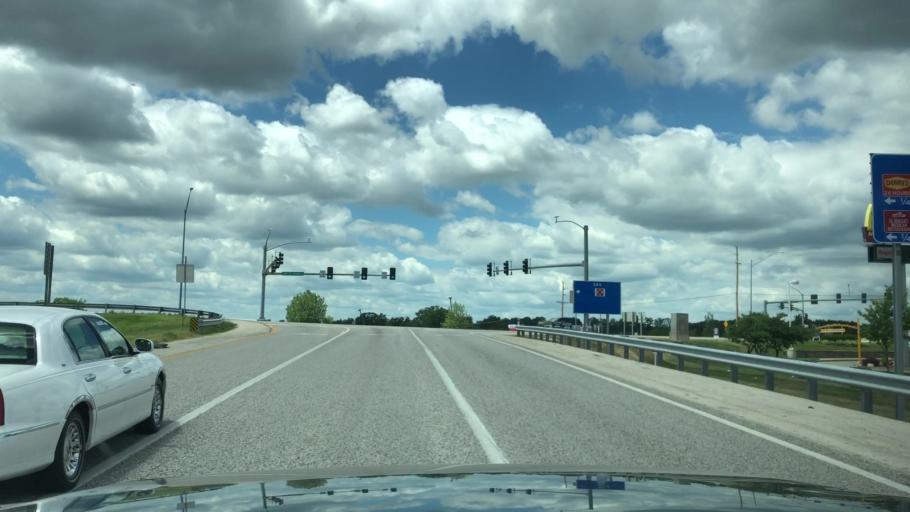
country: US
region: Missouri
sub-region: Saint Charles County
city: Lake Saint Louis
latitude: 38.8044
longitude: -90.7699
